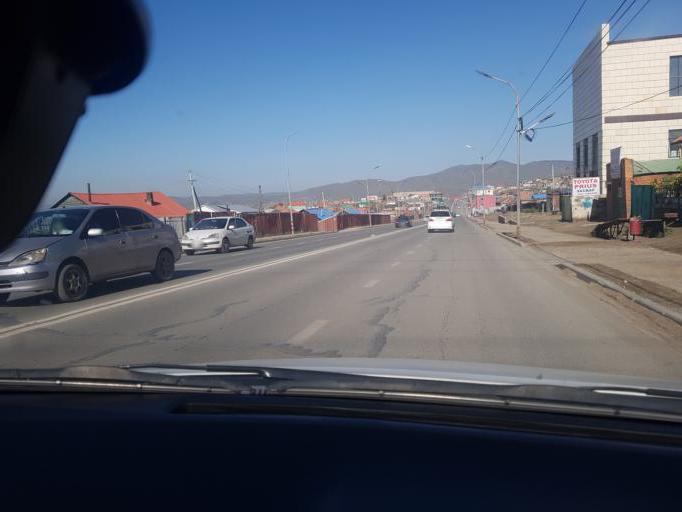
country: MN
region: Ulaanbaatar
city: Ulaanbaatar
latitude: 47.9517
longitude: 106.8578
